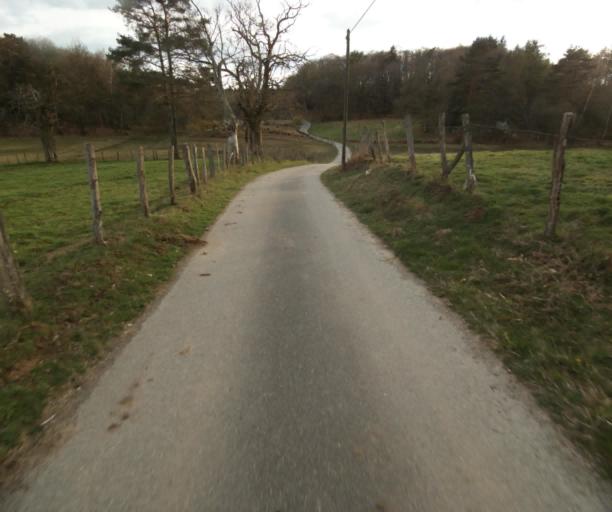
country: FR
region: Limousin
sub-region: Departement de la Correze
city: Argentat
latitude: 45.2278
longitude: 1.9487
